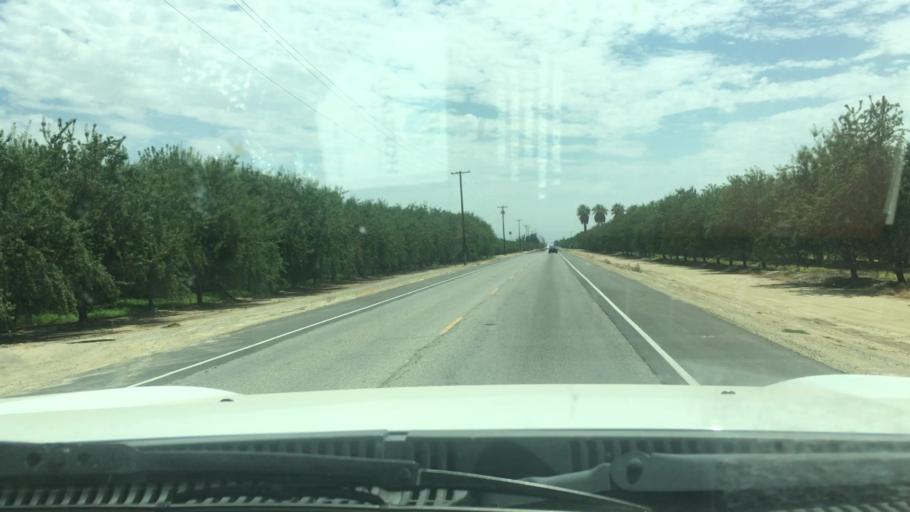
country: US
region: California
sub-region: Kern County
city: Wasco
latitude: 35.5580
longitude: -119.3452
